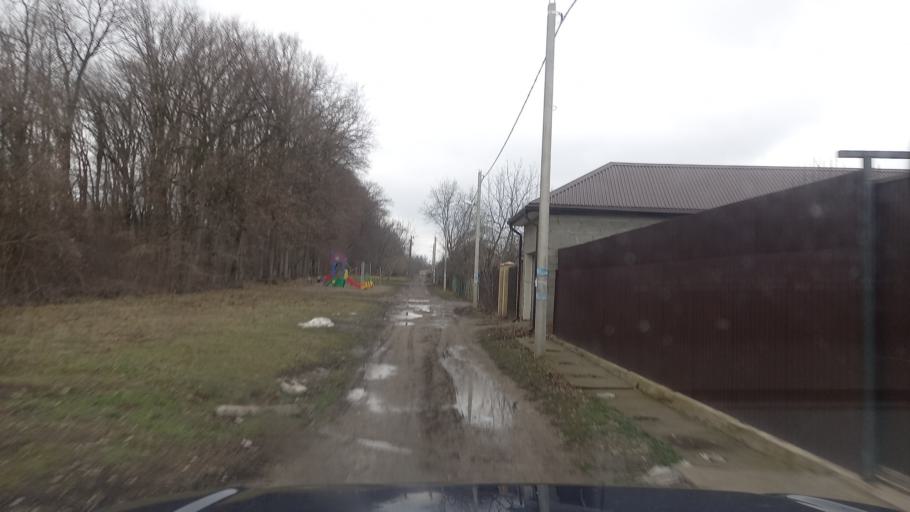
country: RU
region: Krasnodarskiy
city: Pashkovskiy
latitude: 45.0519
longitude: 39.1771
